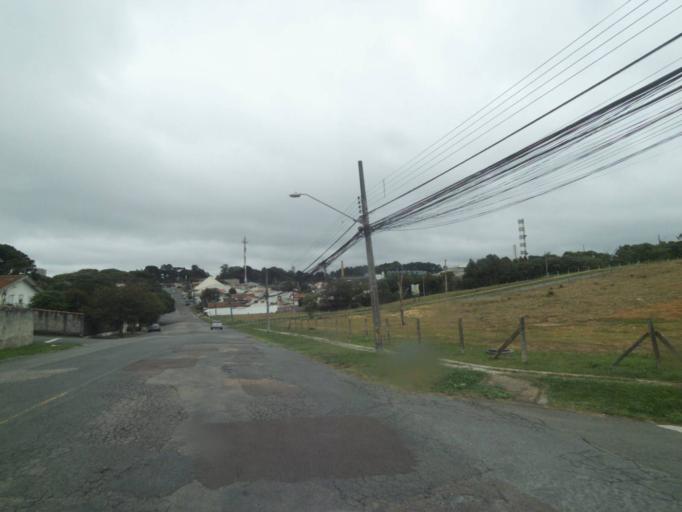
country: BR
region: Parana
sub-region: Curitiba
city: Curitiba
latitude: -25.4267
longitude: -49.3463
